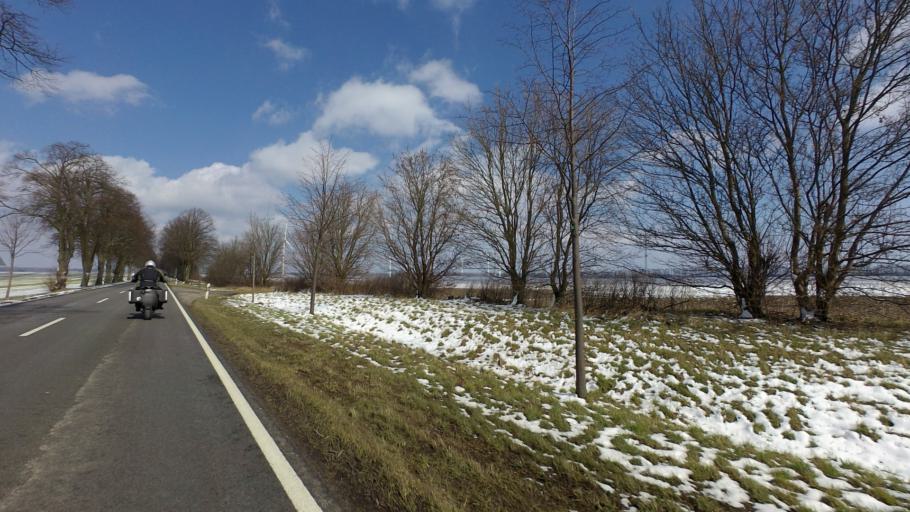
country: DE
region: Brandenburg
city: Eberswalde
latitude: 52.7481
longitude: 13.8443
